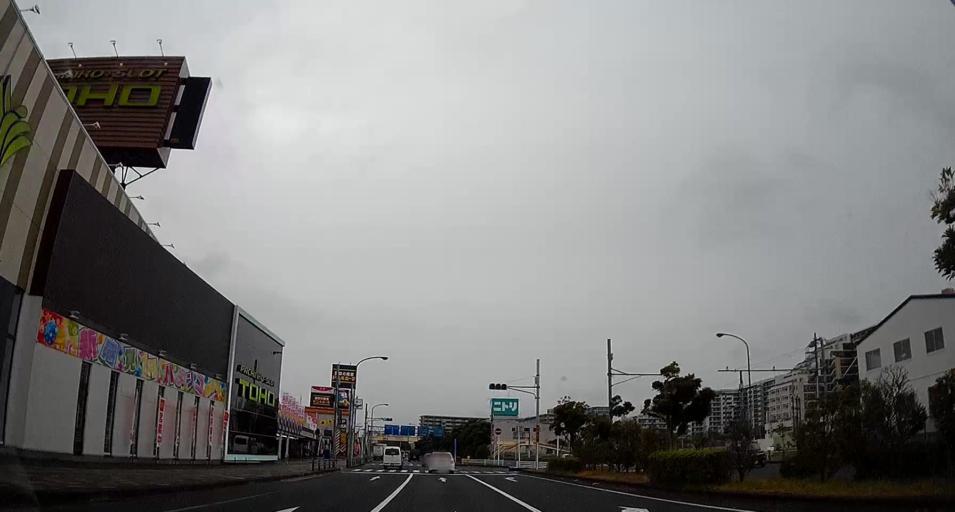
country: JP
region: Chiba
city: Funabashi
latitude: 35.6636
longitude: 140.0425
